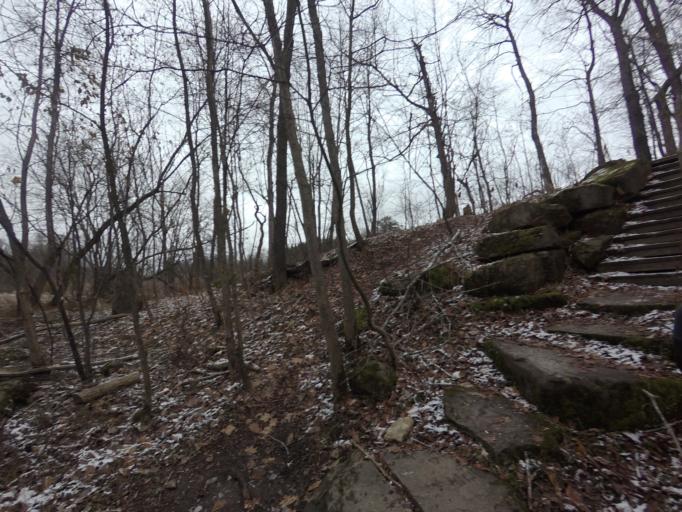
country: CA
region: Ontario
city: Bells Corners
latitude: 45.2484
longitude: -75.7062
